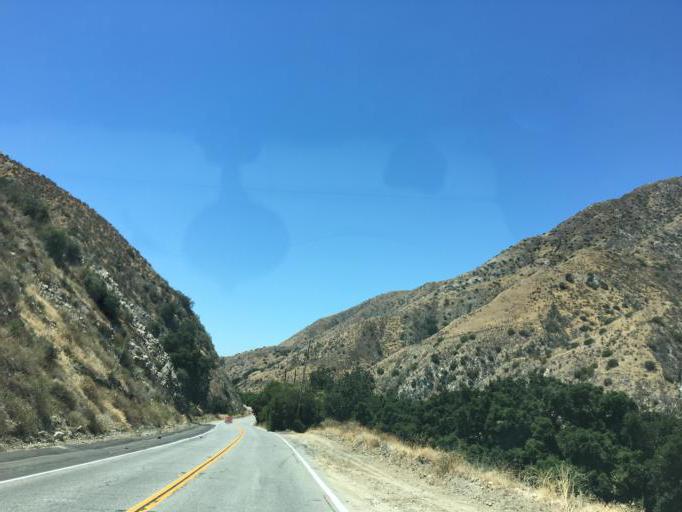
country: US
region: California
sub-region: Los Angeles County
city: La Crescenta-Montrose
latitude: 34.2987
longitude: -118.2789
